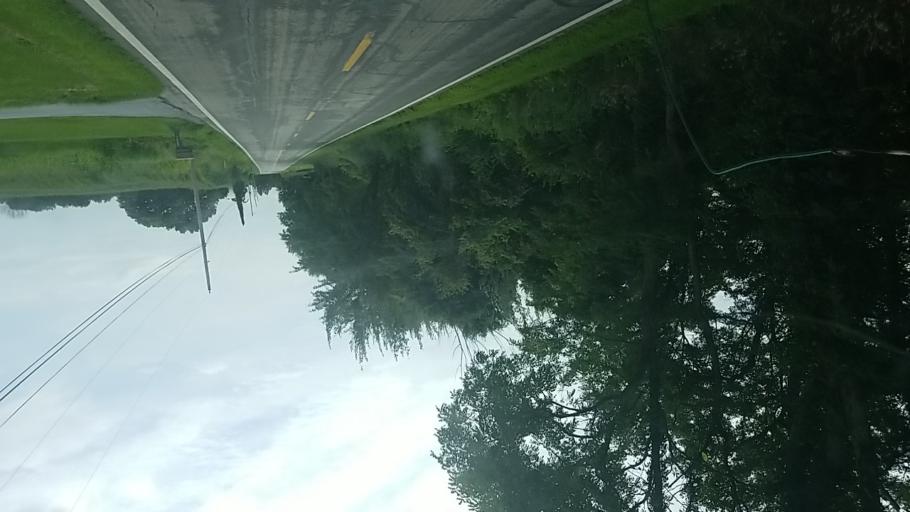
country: US
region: Ohio
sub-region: Franklin County
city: New Albany
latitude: 40.1388
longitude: -82.8220
